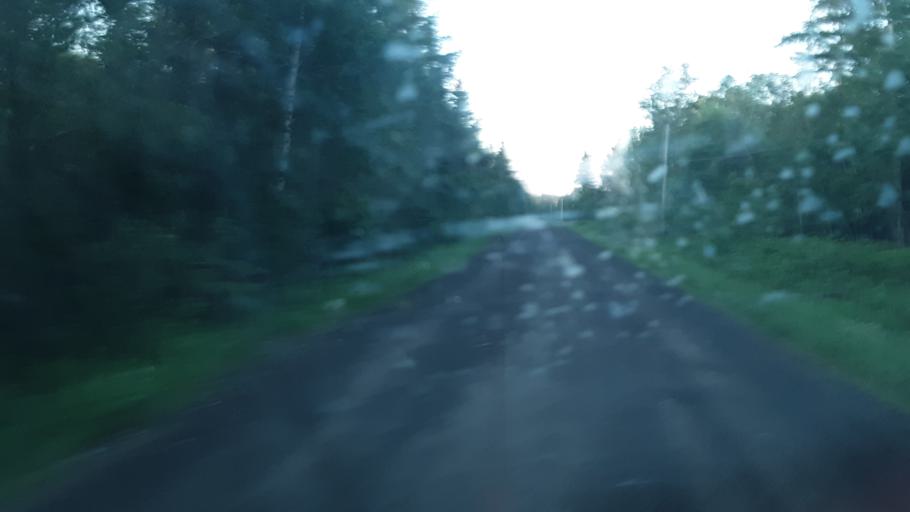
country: US
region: Maine
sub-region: Aroostook County
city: Caribou
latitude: 46.8523
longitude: -68.1346
